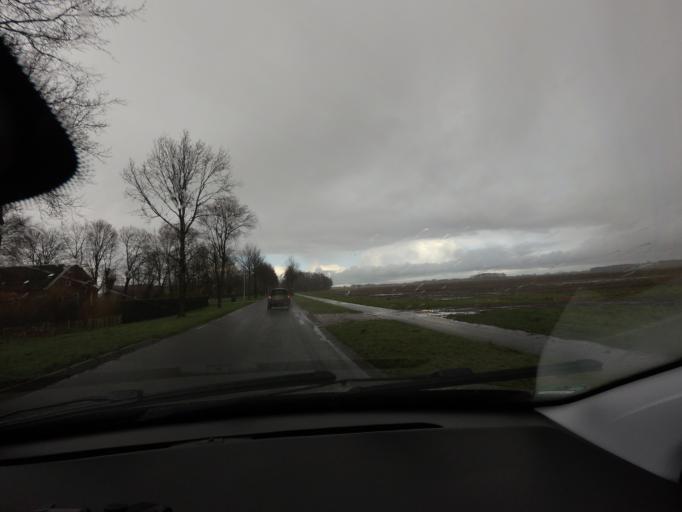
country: NL
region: Drenthe
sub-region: Gemeente Aa en Hunze
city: Anloo
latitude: 53.0223
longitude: 6.7897
